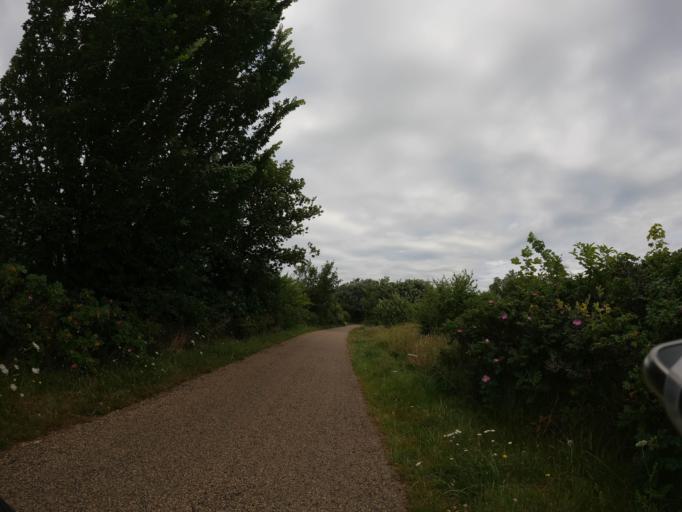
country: DE
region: Schleswig-Holstein
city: Westerland
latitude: 54.9172
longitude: 8.3226
